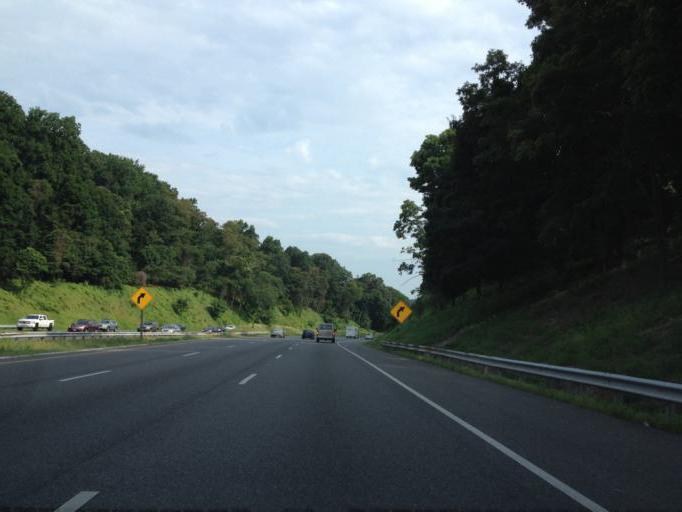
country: US
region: Maryland
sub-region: Baltimore County
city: Mays Chapel
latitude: 39.3916
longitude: -76.6656
